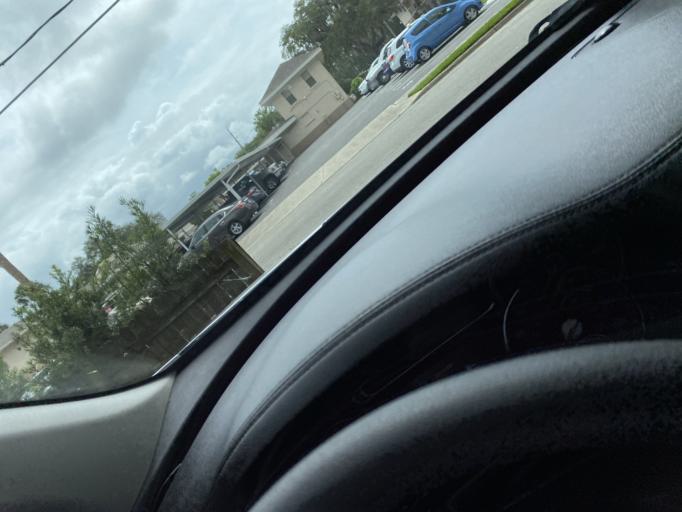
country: US
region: Florida
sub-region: Seminole County
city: Sanford
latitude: 28.8108
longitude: -81.2614
